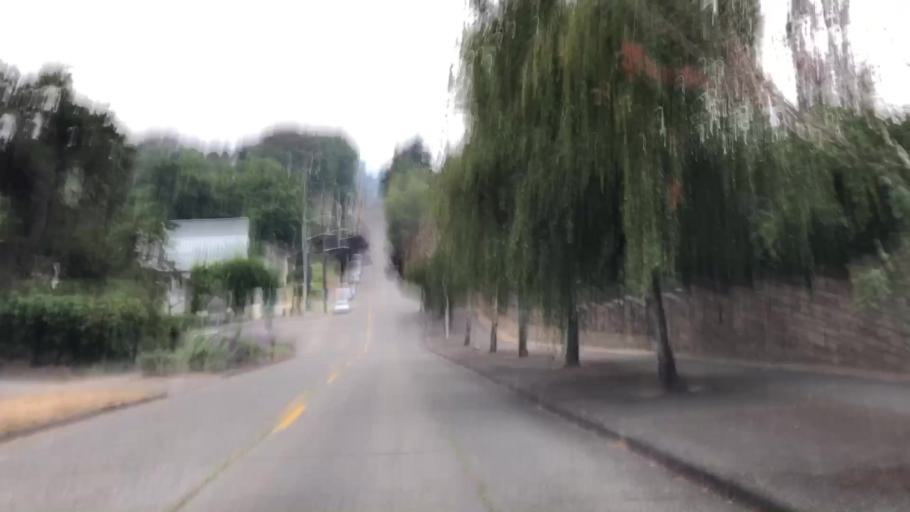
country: US
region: Washington
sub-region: King County
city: Yarrow Point
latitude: 47.6612
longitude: -122.2732
